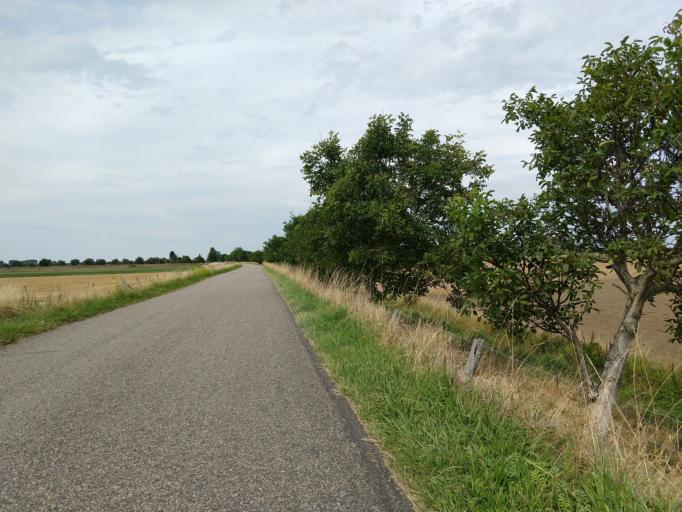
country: NL
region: Zeeland
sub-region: Gemeente Borsele
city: Borssele
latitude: 51.4768
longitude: 3.7412
